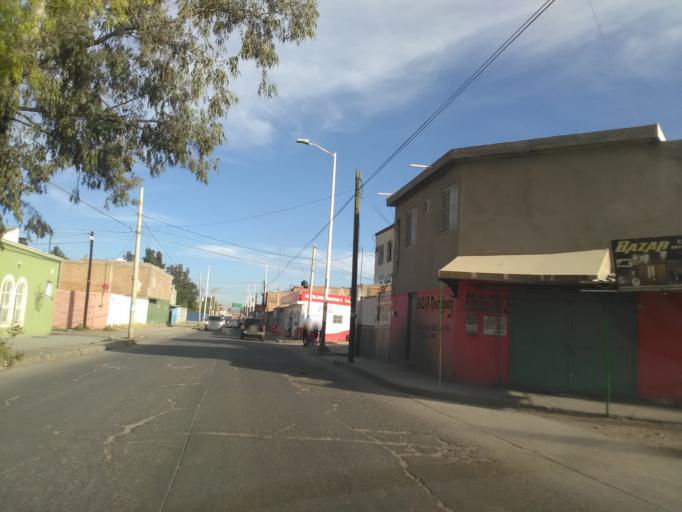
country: MX
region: Durango
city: Victoria de Durango
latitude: 24.0233
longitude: -104.6268
